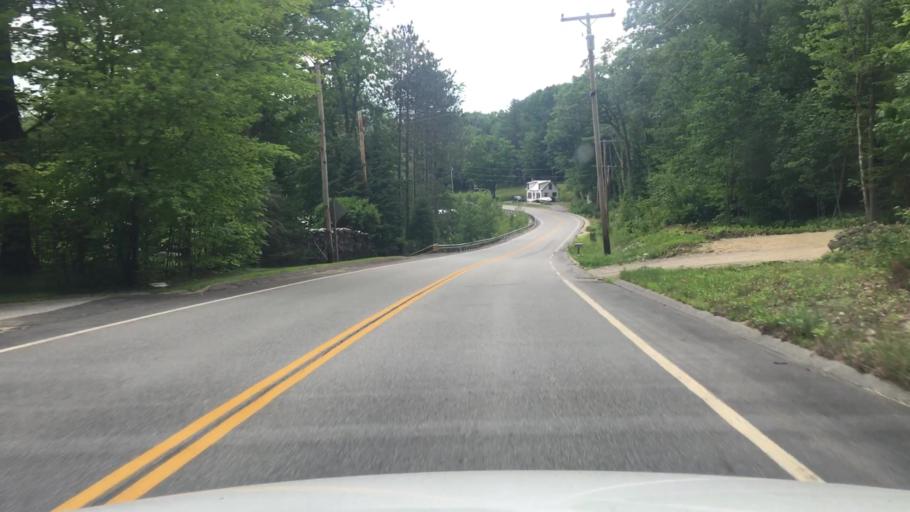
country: US
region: Maine
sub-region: Oxford County
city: Paris
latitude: 44.3695
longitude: -70.4653
